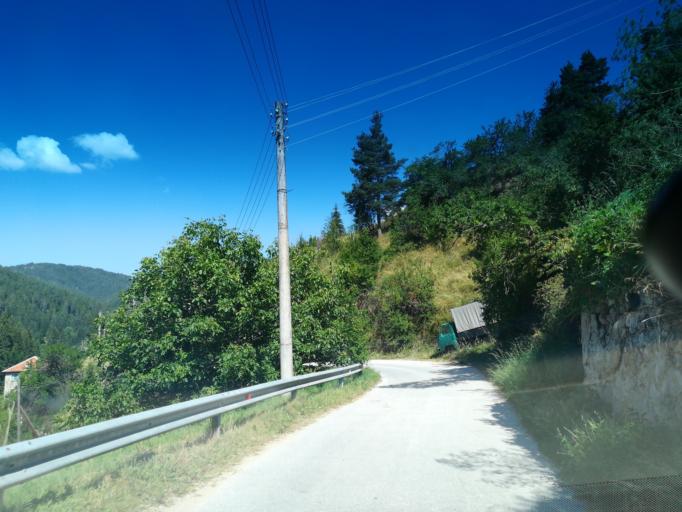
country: BG
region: Smolyan
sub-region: Obshtina Smolyan
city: Smolyan
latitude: 41.6565
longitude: 24.8265
